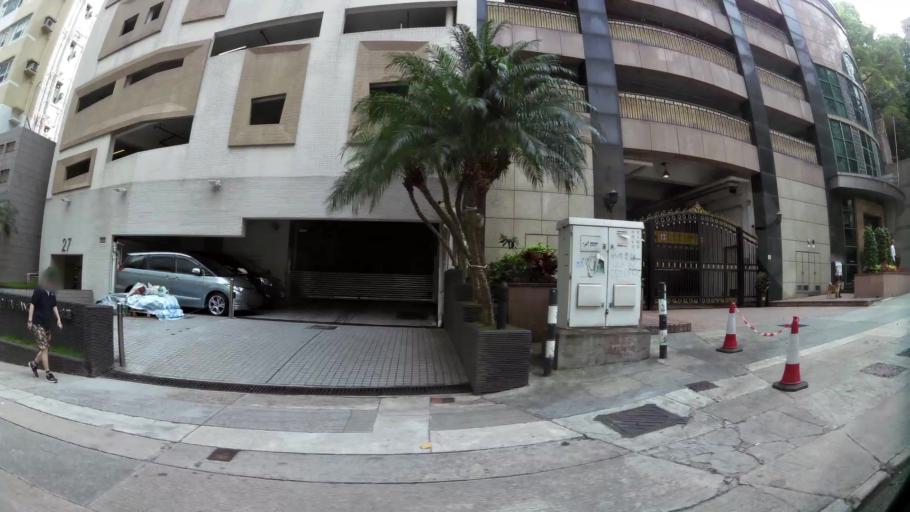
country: HK
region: Wanchai
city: Wan Chai
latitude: 22.2757
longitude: 114.1932
